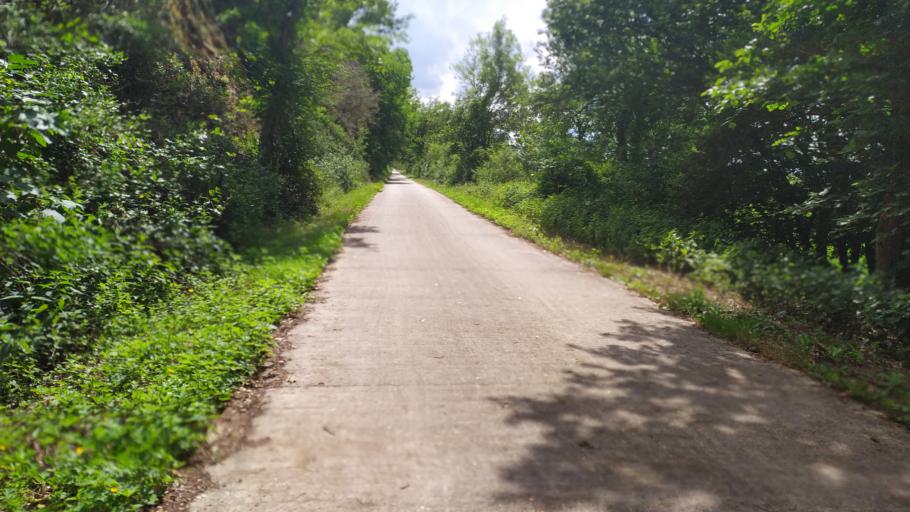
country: BE
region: Wallonia
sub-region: Province du Luxembourg
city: Wellin
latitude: 50.1545
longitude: 5.1271
